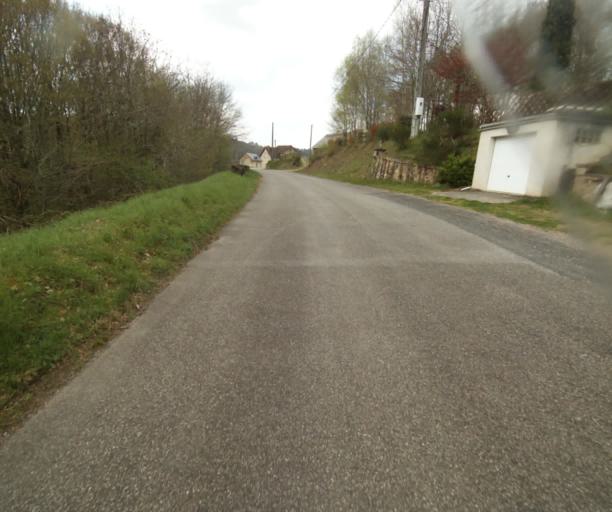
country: FR
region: Limousin
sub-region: Departement de la Correze
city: Naves
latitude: 45.3092
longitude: 1.7992
